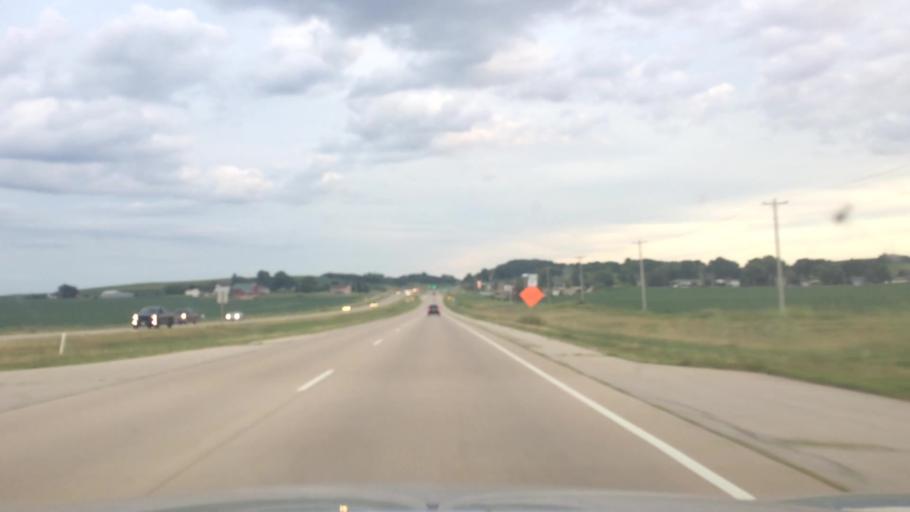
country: US
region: Wisconsin
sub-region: Dane County
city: Middleton
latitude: 43.1465
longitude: -89.5235
